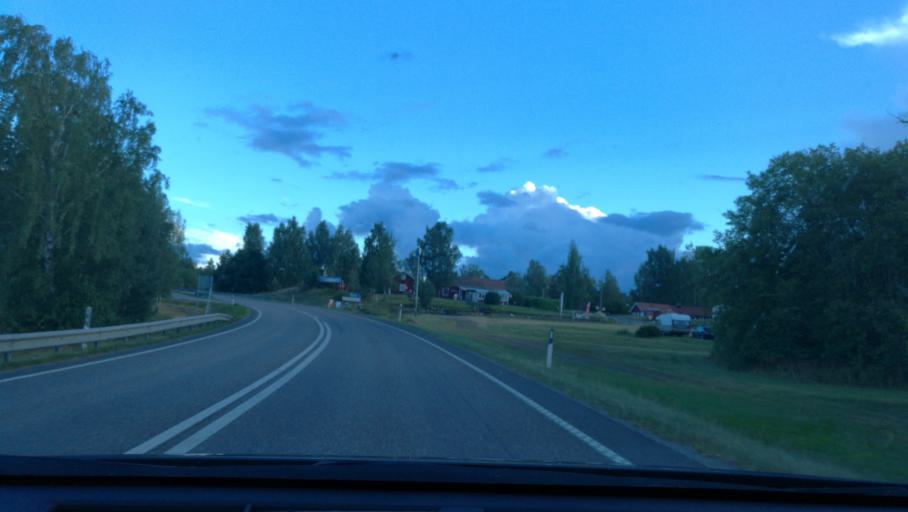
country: SE
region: Vaestmanland
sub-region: Kungsors Kommun
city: Kungsoer
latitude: 59.2409
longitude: 16.1006
